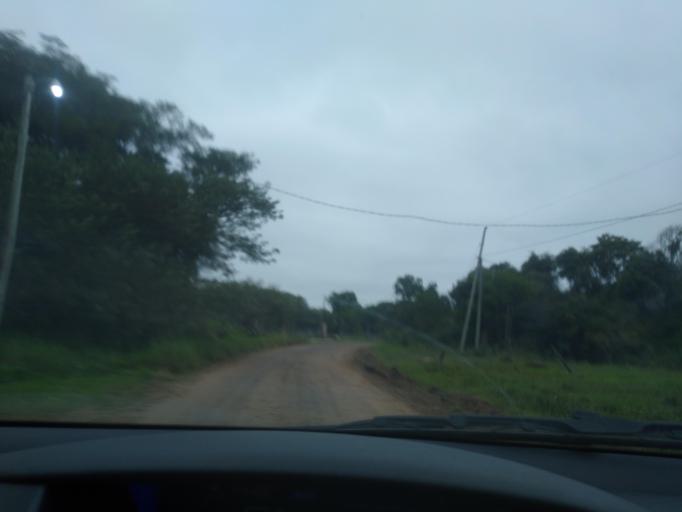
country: AR
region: Chaco
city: Colonia Benitez
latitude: -27.3325
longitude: -58.9645
